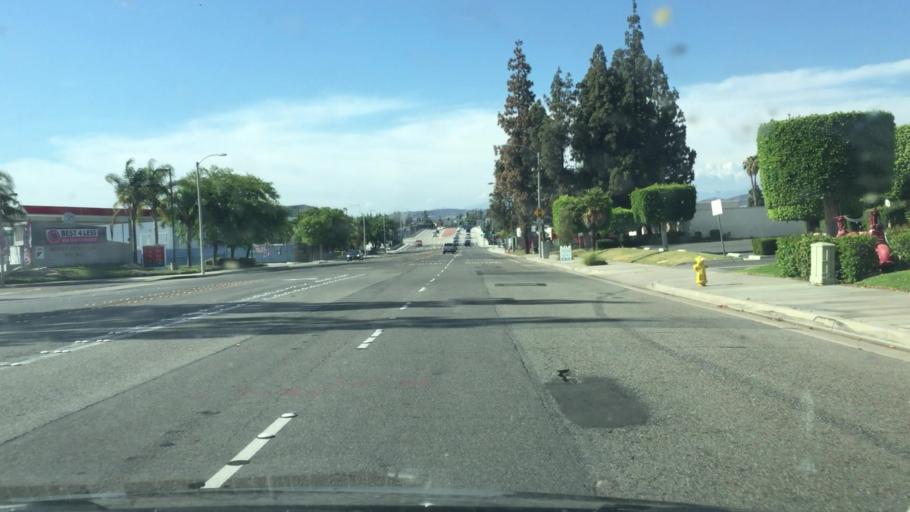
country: US
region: California
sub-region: Orange County
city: Yorba Linda
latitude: 33.8616
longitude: -117.8184
